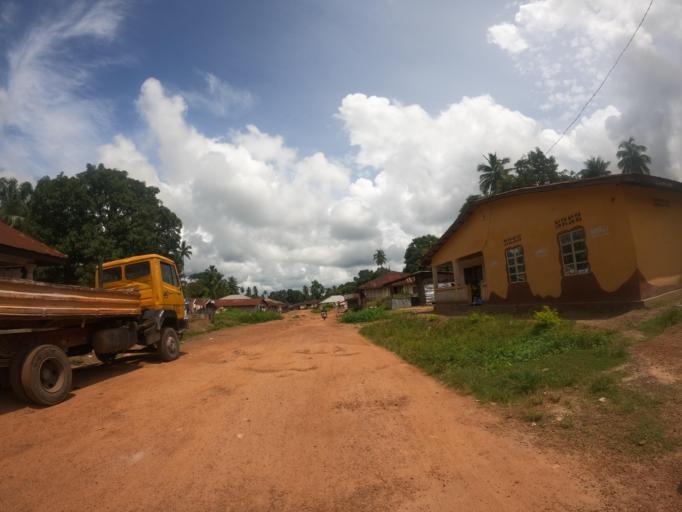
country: SL
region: Northern Province
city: Makeni
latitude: 8.8980
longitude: -12.0582
